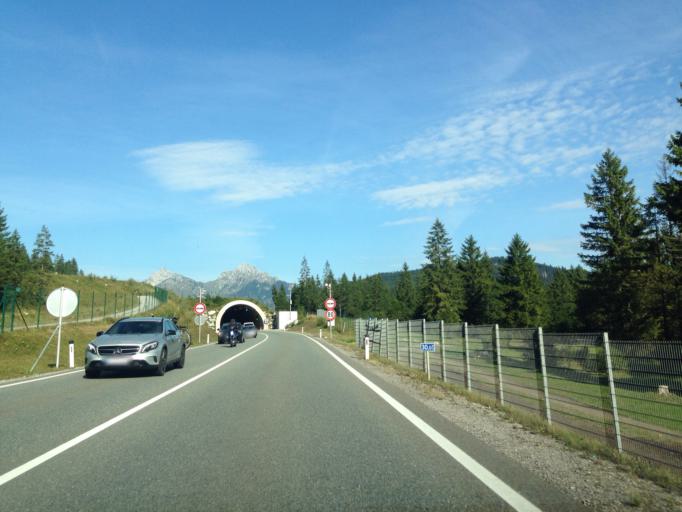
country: AT
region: Tyrol
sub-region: Politischer Bezirk Reutte
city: Heiterwang
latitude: 47.4388
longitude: 10.7510
